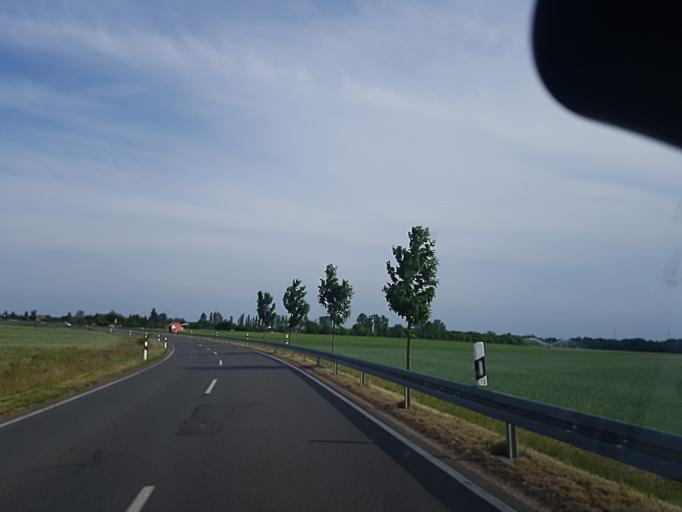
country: DE
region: Saxony-Anhalt
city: Seyda
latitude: 51.8811
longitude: 12.8937
